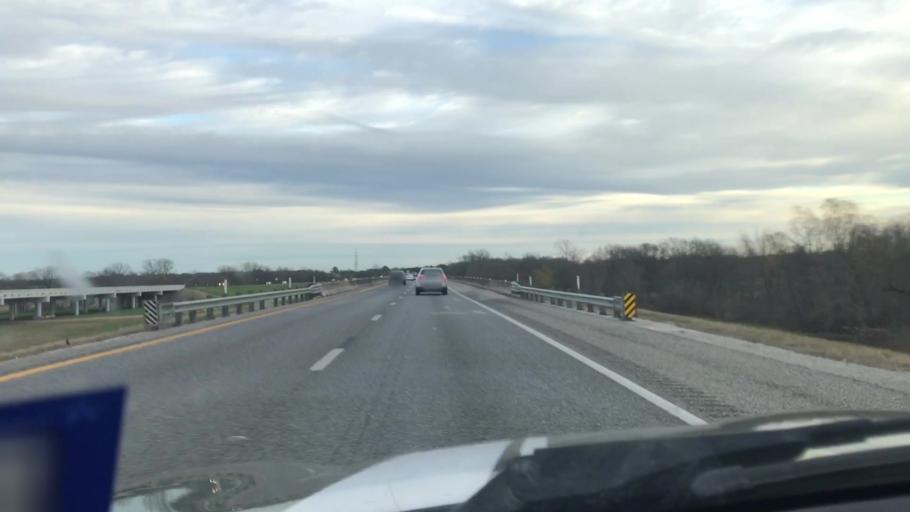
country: US
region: Texas
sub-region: Waller County
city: Hempstead
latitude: 30.1299
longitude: -96.1569
